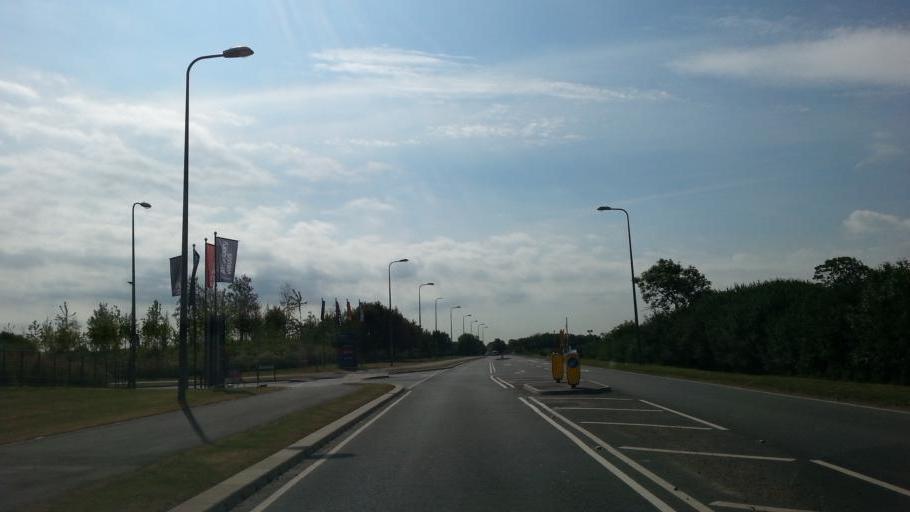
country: GB
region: England
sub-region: Cambridgeshire
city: Great Stukeley
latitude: 52.3690
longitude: -0.2351
